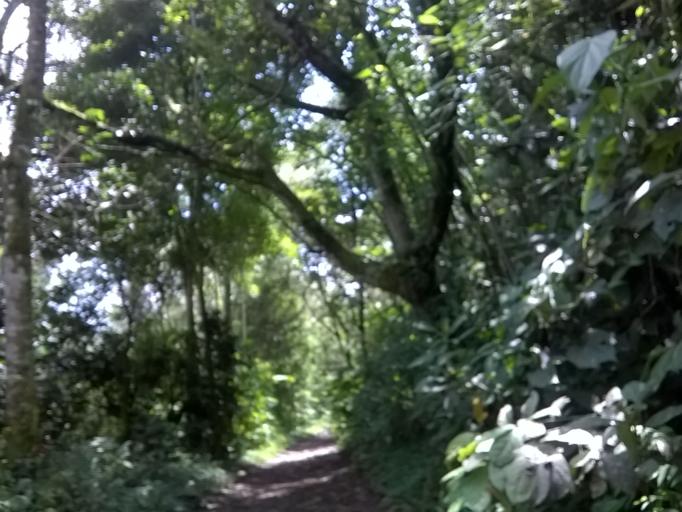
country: CO
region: Quindio
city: Salento
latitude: 4.6473
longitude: -75.5879
